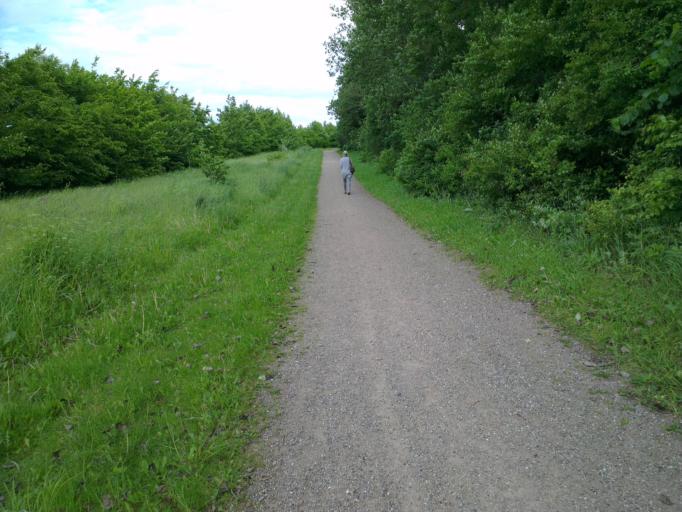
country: DK
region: Capital Region
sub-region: Frederikssund Kommune
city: Frederikssund
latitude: 55.8645
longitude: 12.0699
